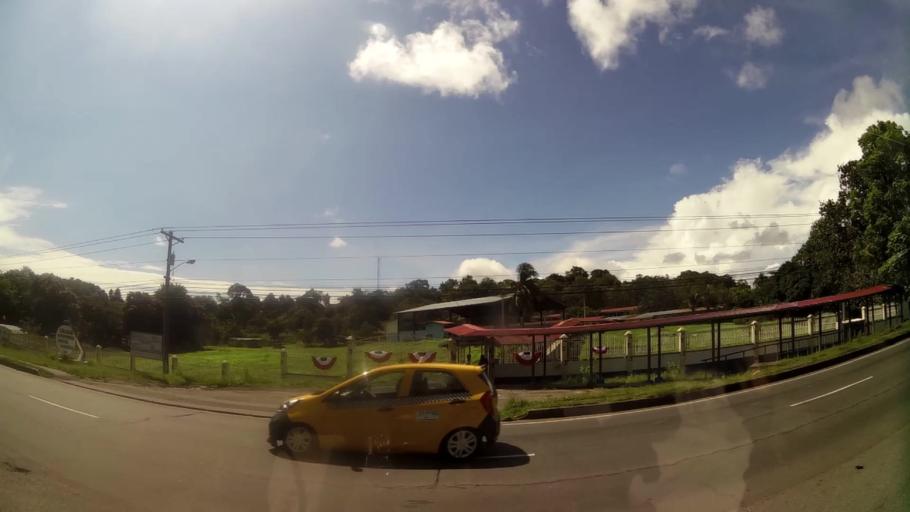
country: PA
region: Panama
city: Chame
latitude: 8.5819
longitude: -79.8843
